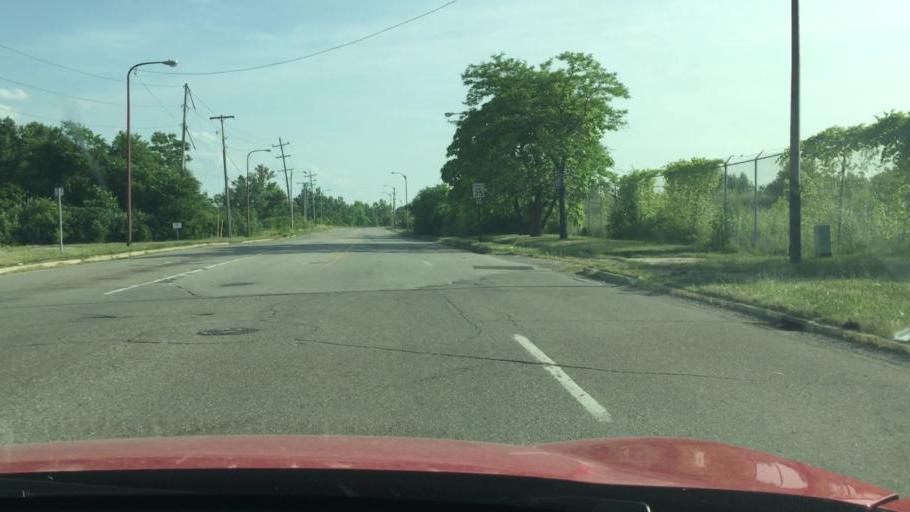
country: US
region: Michigan
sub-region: Genesee County
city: Flint
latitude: 43.0389
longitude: -83.6797
